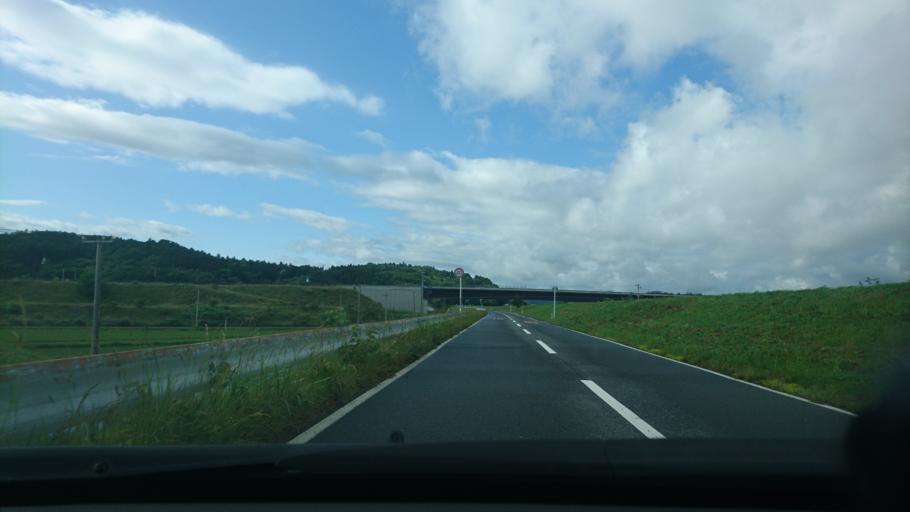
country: JP
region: Miyagi
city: Wakuya
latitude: 38.6956
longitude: 141.2851
